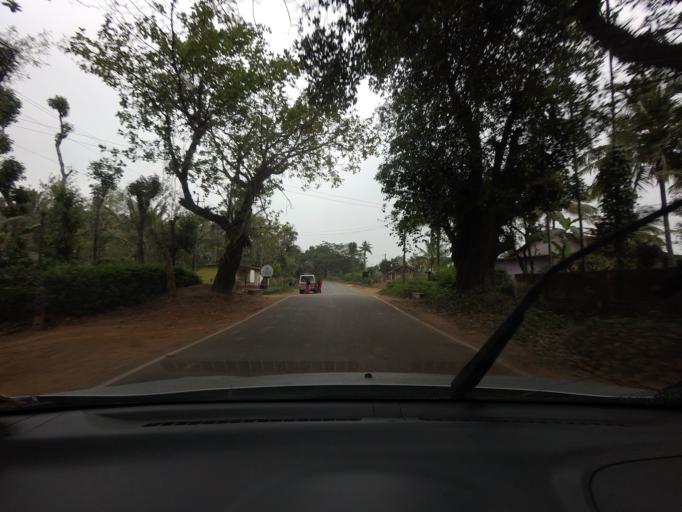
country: IN
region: Karnataka
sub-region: Hassan
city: Sakleshpur
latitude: 12.9940
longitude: 75.7067
